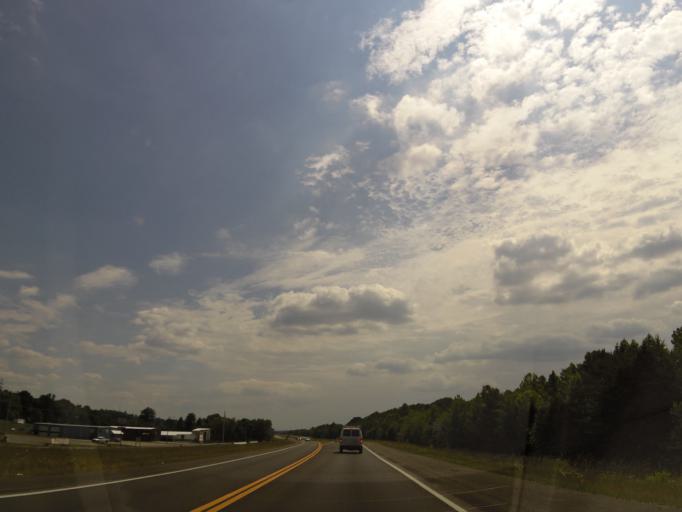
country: US
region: Tennessee
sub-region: Marion County
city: Jasper
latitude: 35.0810
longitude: -85.6082
